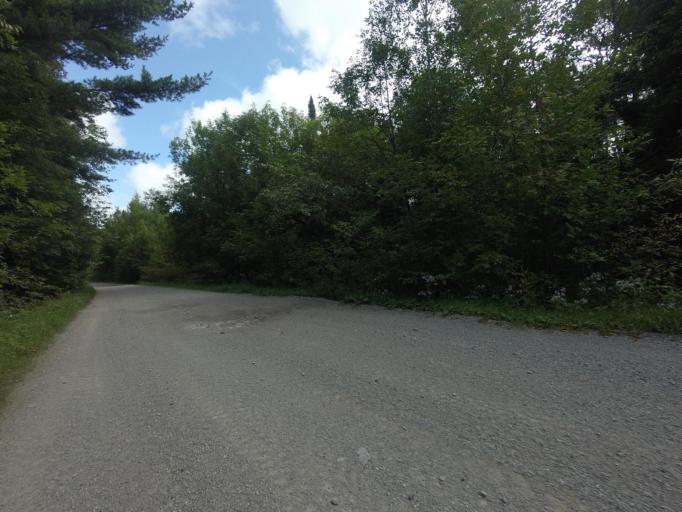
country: CA
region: Ontario
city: Omemee
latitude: 44.7727
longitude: -78.6549
